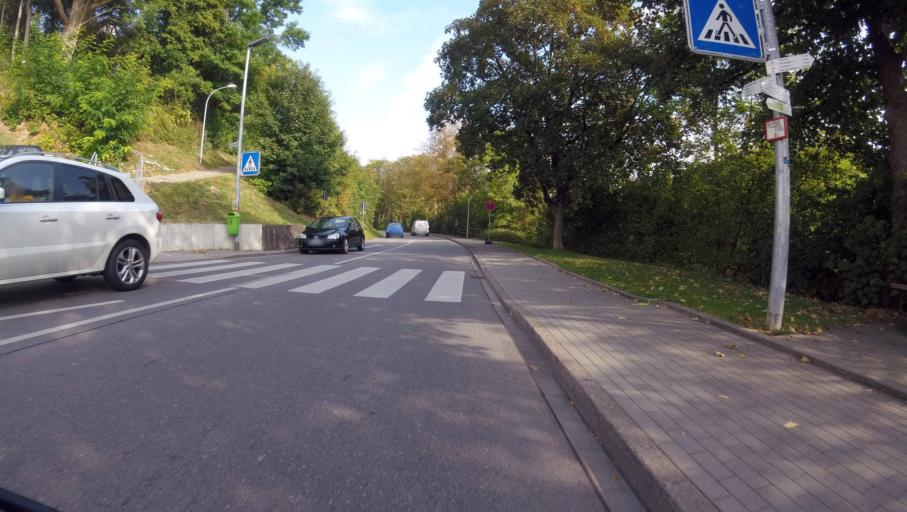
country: DE
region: Baden-Wuerttemberg
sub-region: Karlsruhe Region
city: Nagold
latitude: 48.5336
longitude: 8.7227
